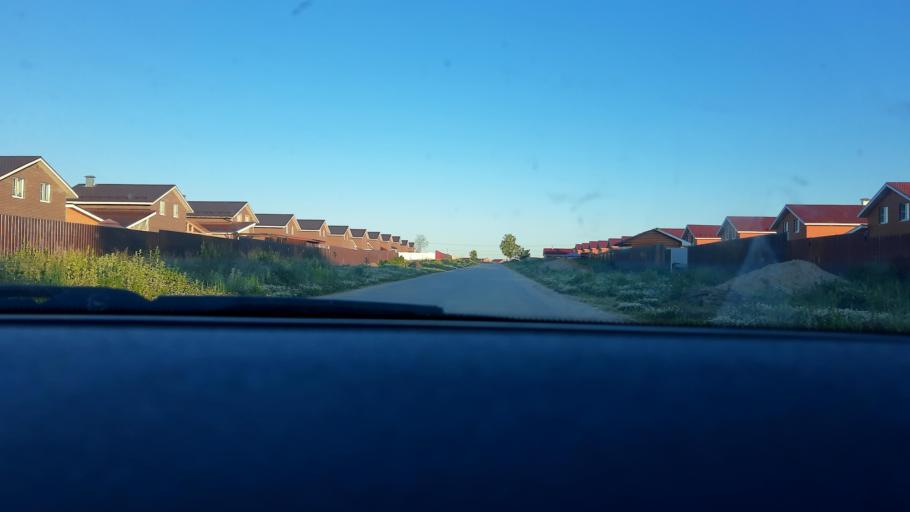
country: RU
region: Nizjnij Novgorod
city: Afonino
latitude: 56.1970
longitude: 44.0797
